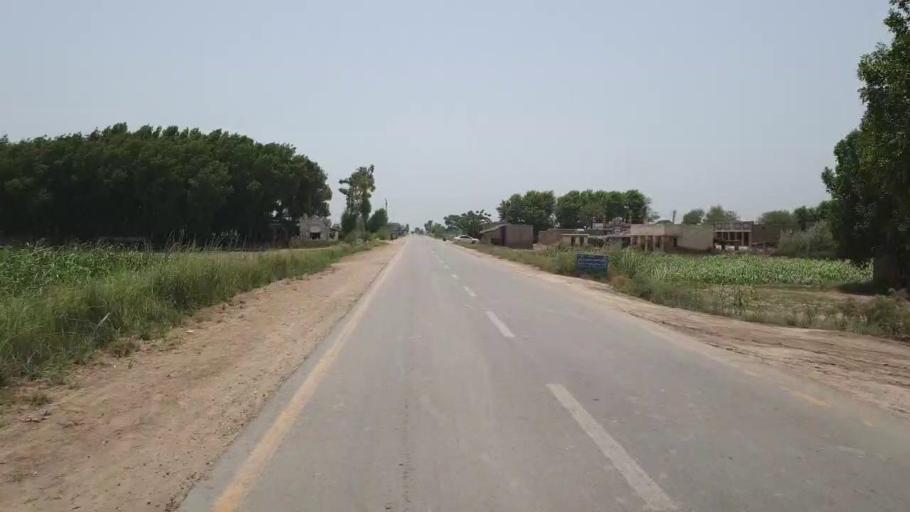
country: PK
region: Sindh
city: Moro
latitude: 26.5987
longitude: 68.1015
